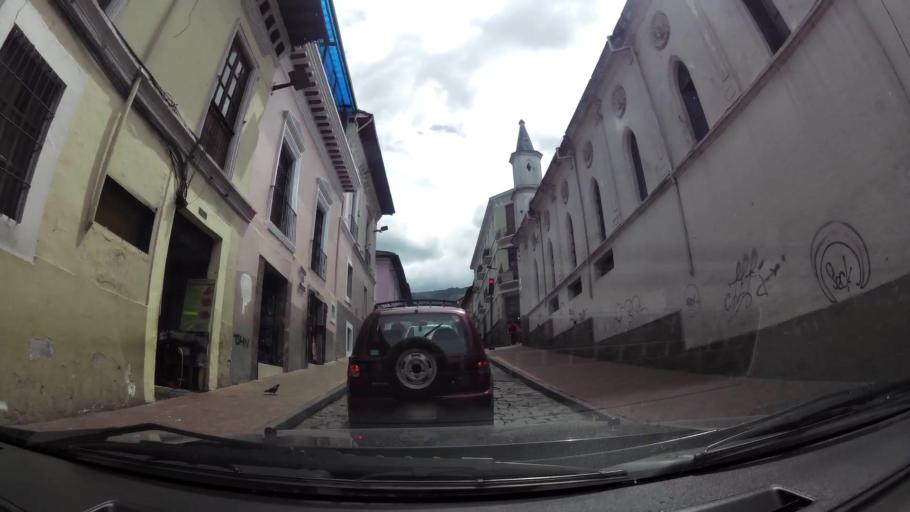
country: EC
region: Pichincha
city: Quito
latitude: -0.2174
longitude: -78.5124
